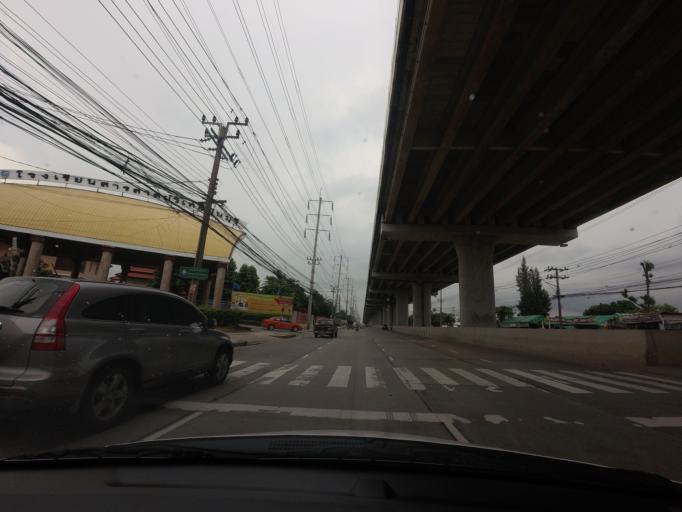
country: TH
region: Bangkok
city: Min Buri
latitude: 13.8156
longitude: 100.7491
